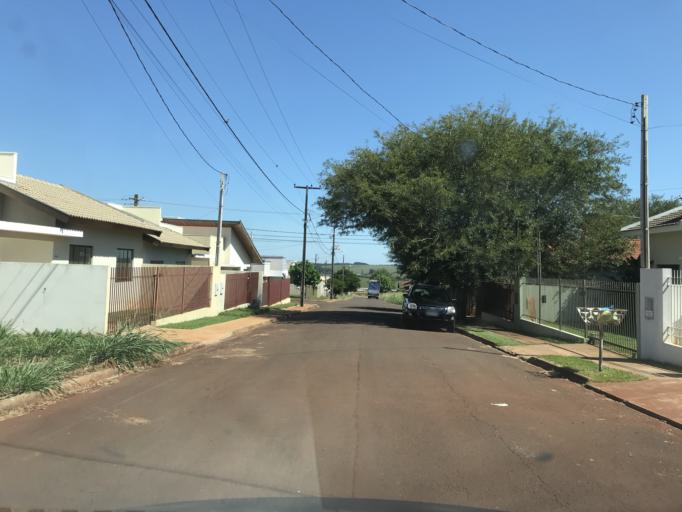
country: BR
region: Parana
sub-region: Palotina
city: Palotina
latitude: -24.3019
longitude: -53.8384
